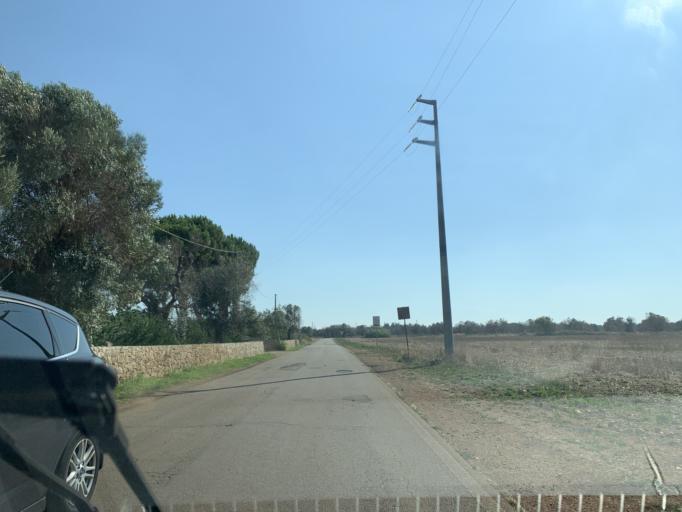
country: IT
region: Apulia
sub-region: Provincia di Lecce
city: Copertino
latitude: 40.2602
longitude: 18.0231
